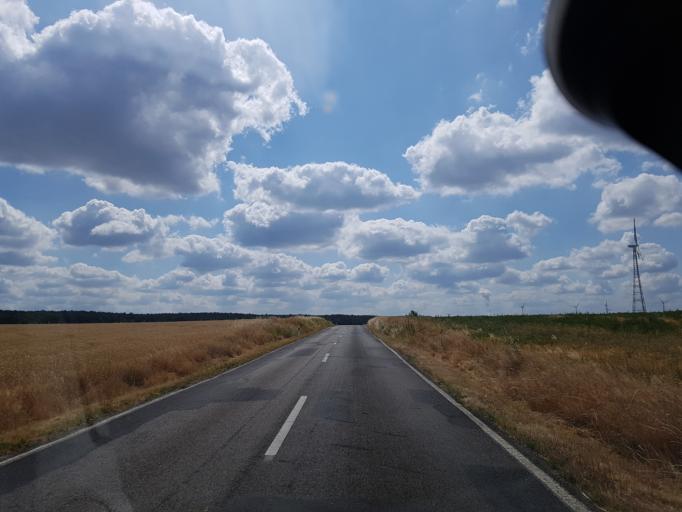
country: DE
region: Brandenburg
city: Drebkau
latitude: 51.6820
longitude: 14.2769
